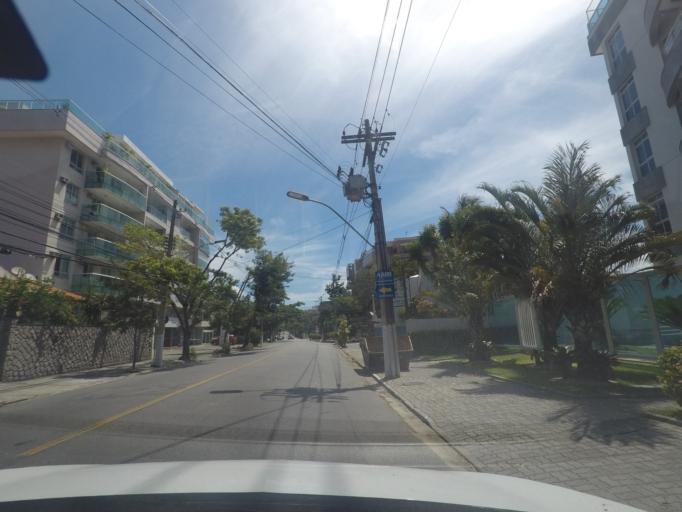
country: BR
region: Rio de Janeiro
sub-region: Niteroi
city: Niteroi
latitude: -22.9159
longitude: -43.0841
